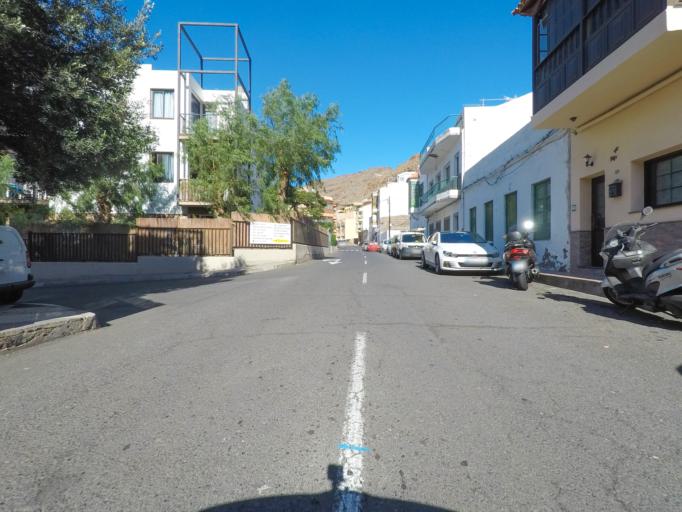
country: ES
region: Canary Islands
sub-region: Provincia de Santa Cruz de Tenerife
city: Alajero
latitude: 28.0301
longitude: -17.1974
